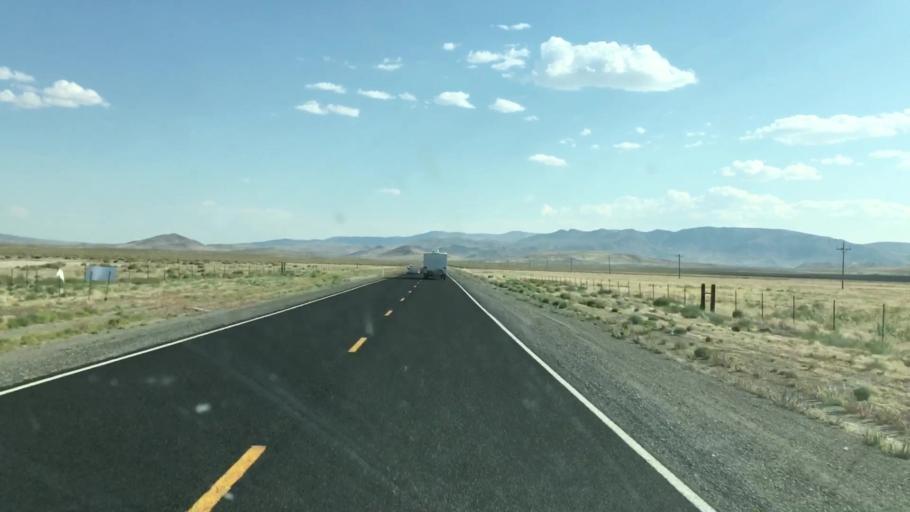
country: US
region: Nevada
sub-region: Lyon County
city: Fernley
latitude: 39.6796
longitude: -119.3340
